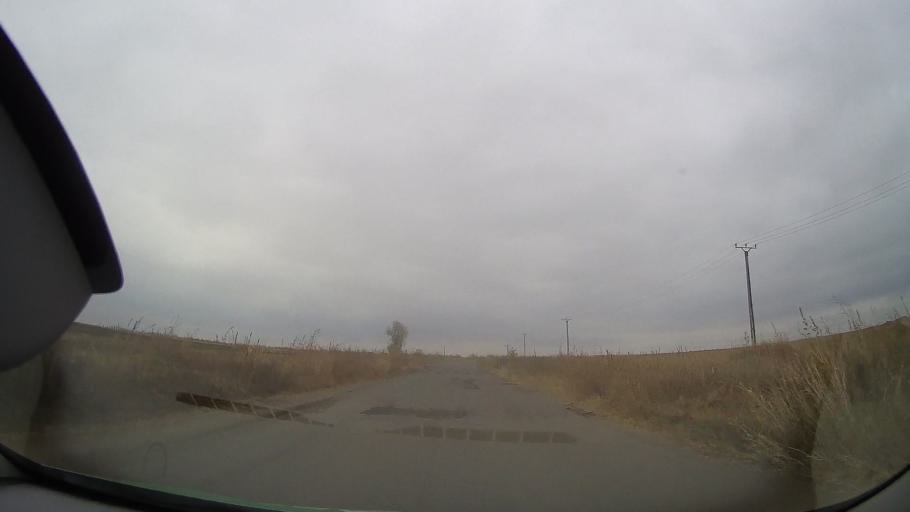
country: RO
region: Braila
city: Dudesti
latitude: 44.9319
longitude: 27.4271
